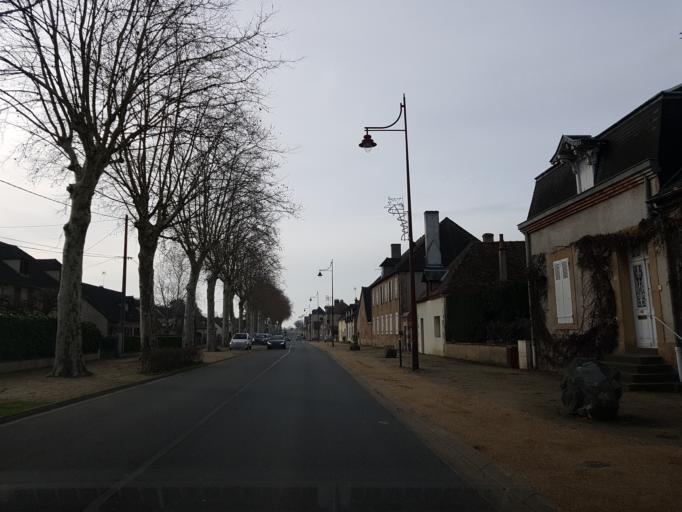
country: FR
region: Auvergne
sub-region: Departement de l'Allier
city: Lusigny
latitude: 46.6101
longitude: 3.5502
